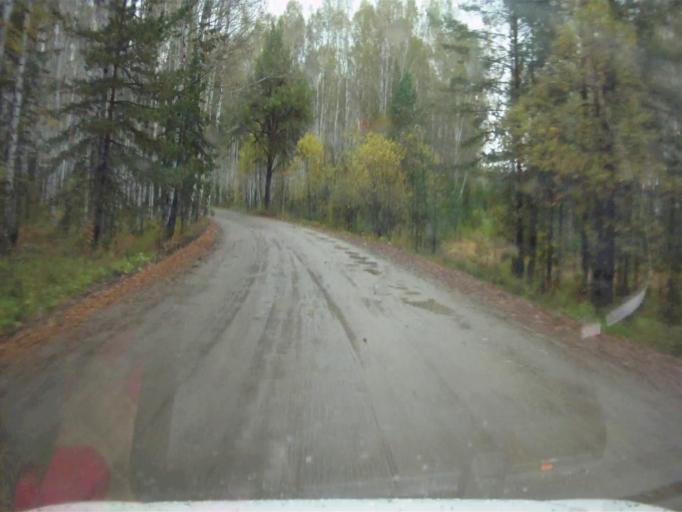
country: RU
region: Chelyabinsk
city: Kyshtym
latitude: 55.8413
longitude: 60.4866
